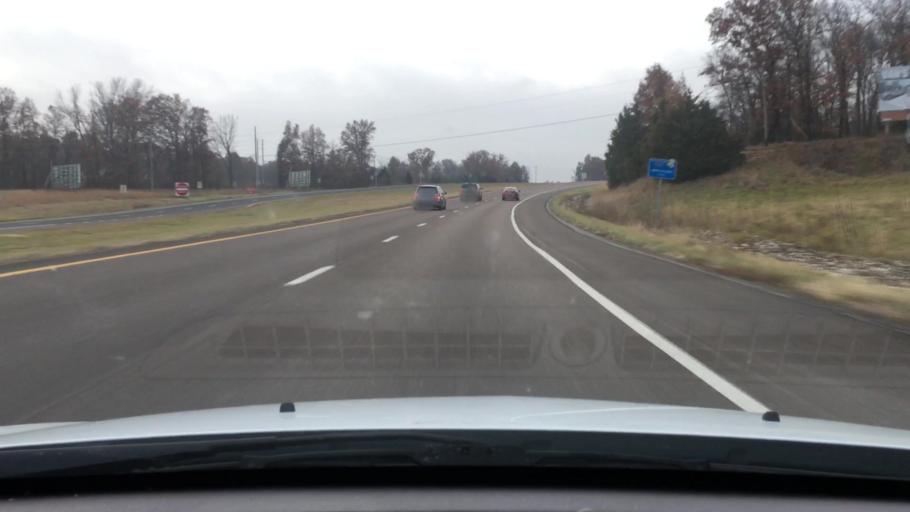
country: US
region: Missouri
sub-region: Callaway County
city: Fulton
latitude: 38.9494
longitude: -91.9402
